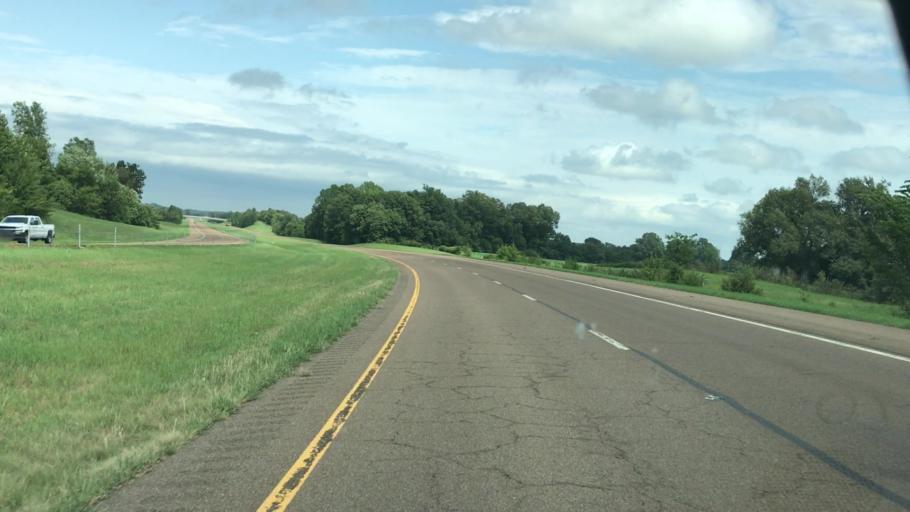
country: US
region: Tennessee
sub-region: Obion County
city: Union City
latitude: 36.4590
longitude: -88.9874
